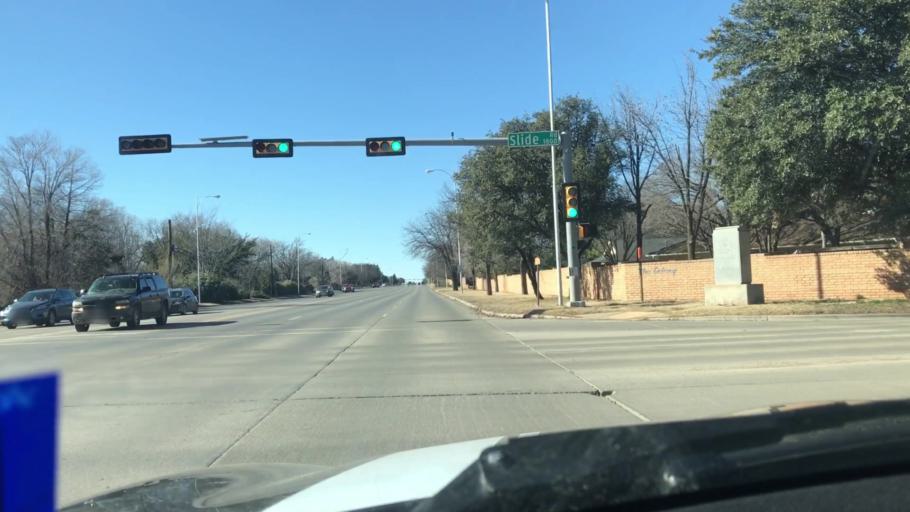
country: US
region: Texas
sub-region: Lubbock County
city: Lubbock
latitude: 33.5779
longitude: -101.9224
